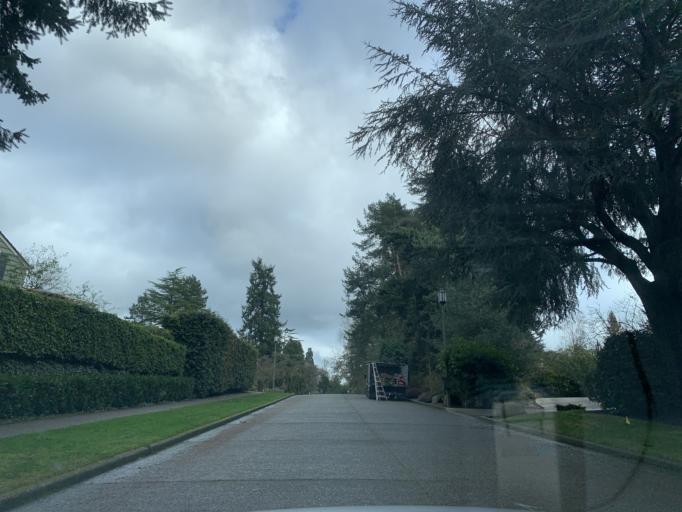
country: US
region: Washington
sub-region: King County
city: Yarrow Point
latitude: 47.6665
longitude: -122.2649
